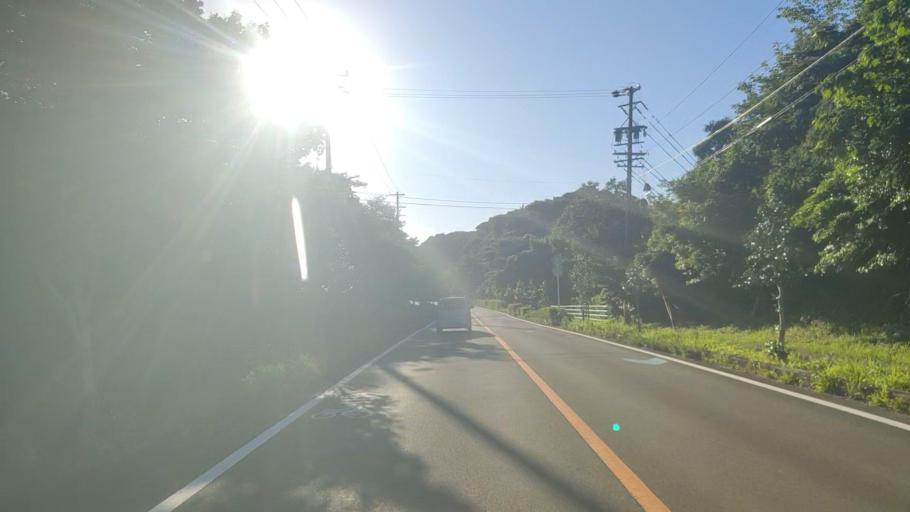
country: JP
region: Mie
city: Toba
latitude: 34.2626
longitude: 136.8272
